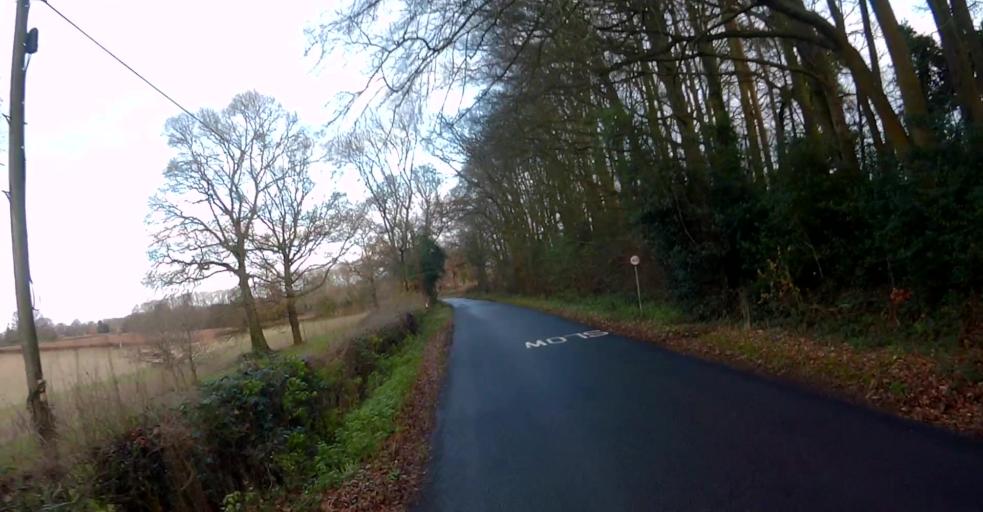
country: GB
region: England
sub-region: Hampshire
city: Old Basing
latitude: 51.1995
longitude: -1.0508
